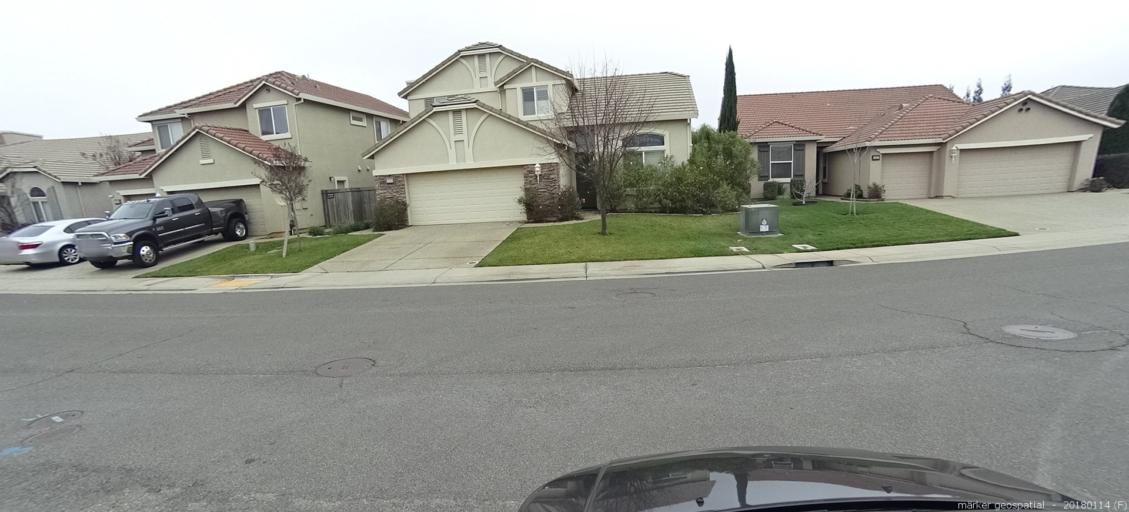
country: US
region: California
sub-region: Sacramento County
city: Gold River
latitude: 38.5472
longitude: -121.2344
